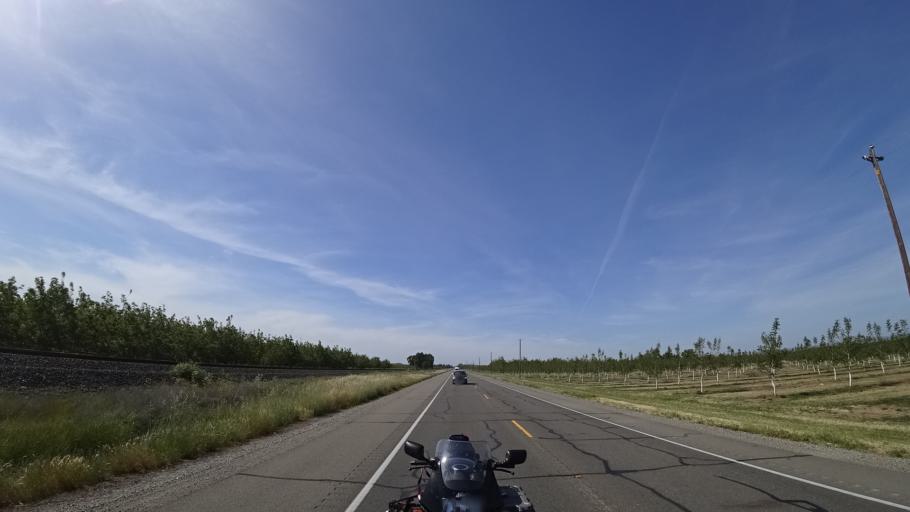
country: US
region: California
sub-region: Tehama County
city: Los Molinos
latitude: 39.9956
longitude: -122.0871
